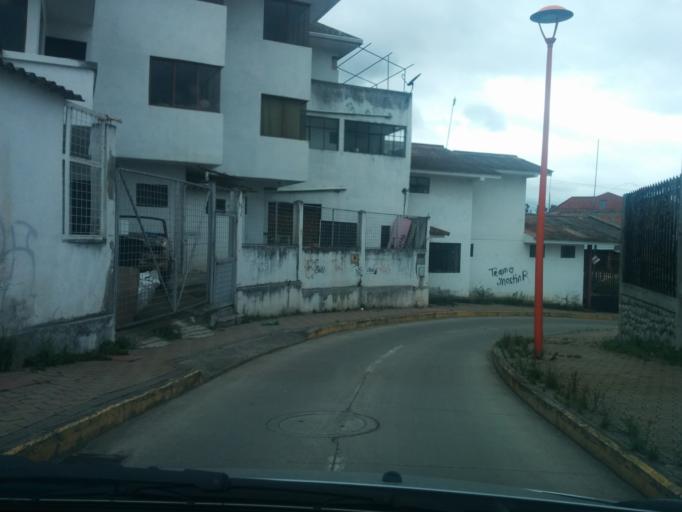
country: EC
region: Azuay
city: Cuenca
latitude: -2.9201
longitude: -79.0641
